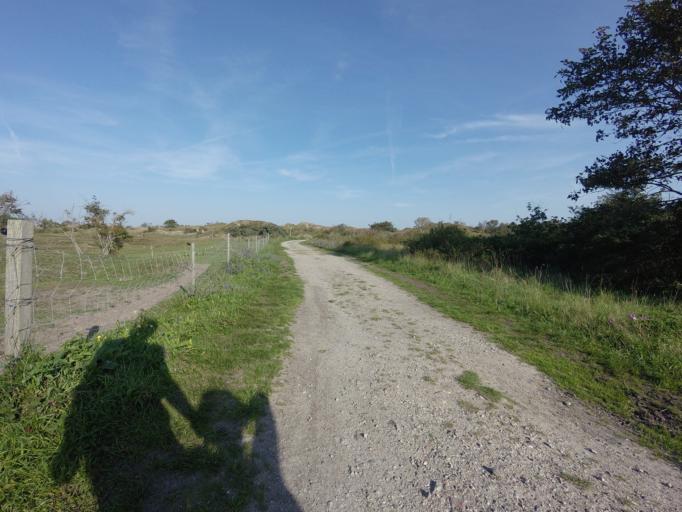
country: NL
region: Friesland
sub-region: Gemeente Schiermonnikoog
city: Schiermonnikoog
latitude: 53.4887
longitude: 6.1804
